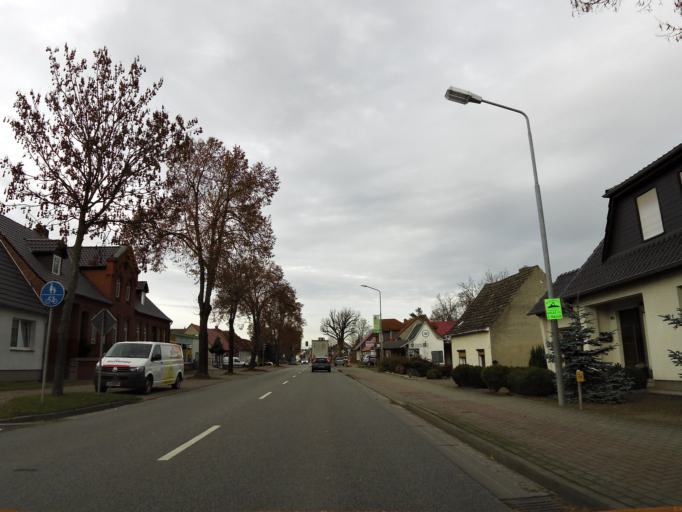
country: DE
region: Saxony-Anhalt
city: Kalbe
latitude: 52.6646
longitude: 11.2803
